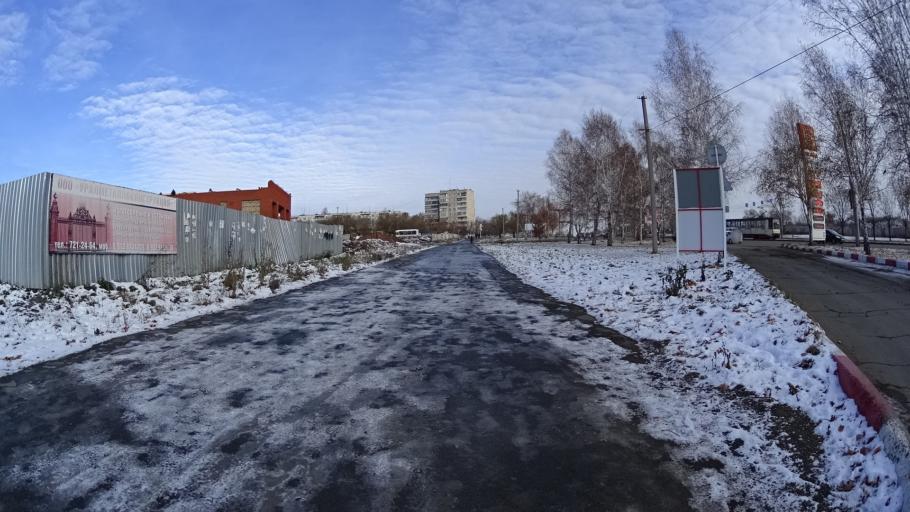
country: RU
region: Chelyabinsk
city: Roshchino
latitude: 55.1882
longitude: 61.3042
